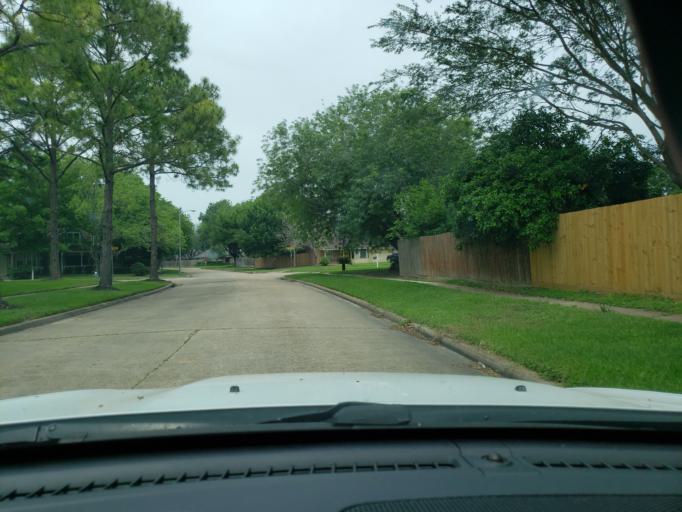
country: US
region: Texas
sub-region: Harris County
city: Jersey Village
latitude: 29.9143
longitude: -95.5732
